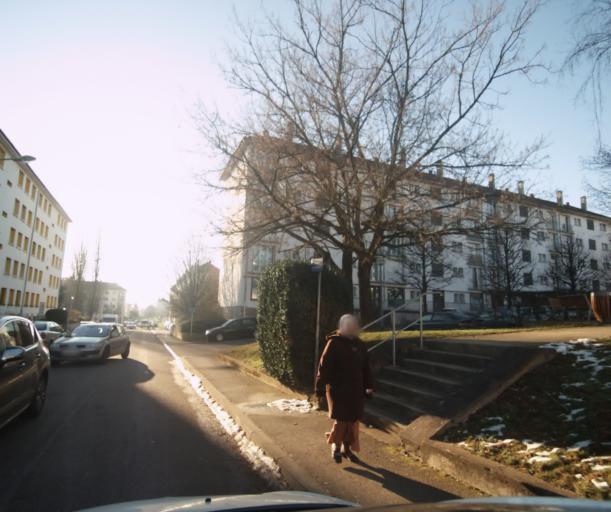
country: FR
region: Franche-Comte
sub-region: Departement du Doubs
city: Besancon
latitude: 47.2611
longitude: 6.0410
